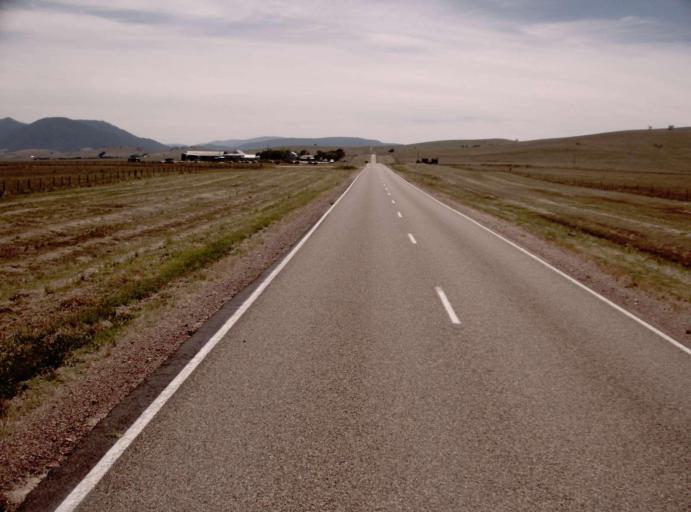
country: AU
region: Victoria
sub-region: Alpine
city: Mount Beauty
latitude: -36.9988
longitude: 147.6755
